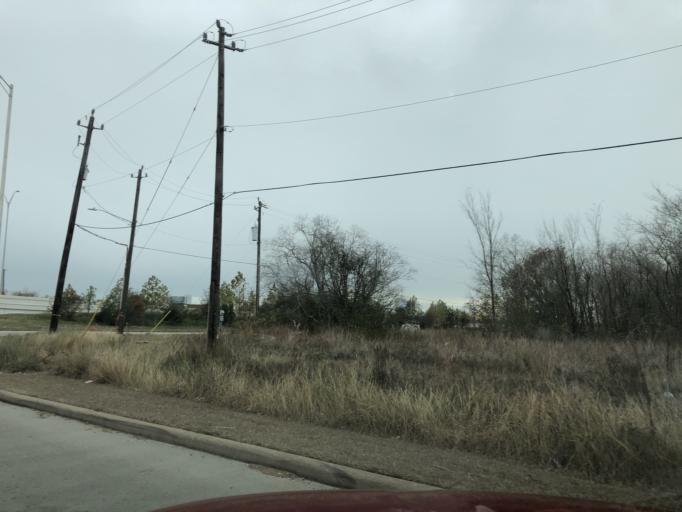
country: US
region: Texas
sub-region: Fort Bend County
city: Missouri City
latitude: 29.6292
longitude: -95.5200
